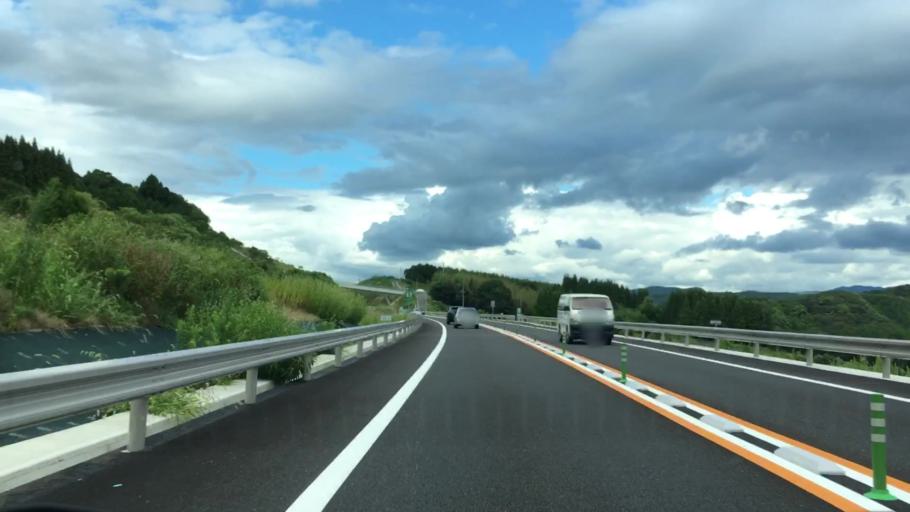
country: JP
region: Saga Prefecture
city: Imaricho-ko
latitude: 33.3184
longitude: 129.9239
